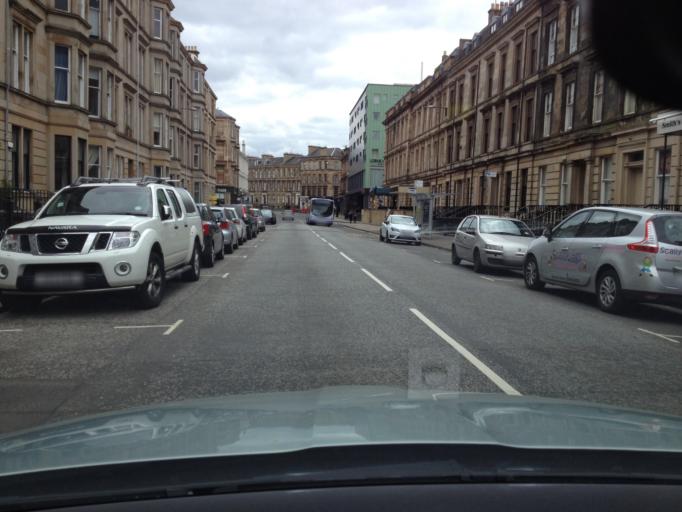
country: GB
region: Scotland
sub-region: Glasgow City
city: Glasgow
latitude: 55.8661
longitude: -4.2863
